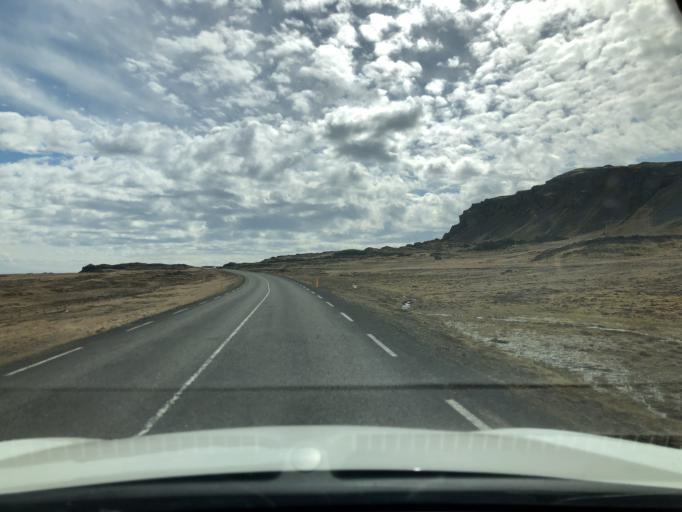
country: IS
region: East
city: Reydarfjoerdur
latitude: 64.6696
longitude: -14.3275
